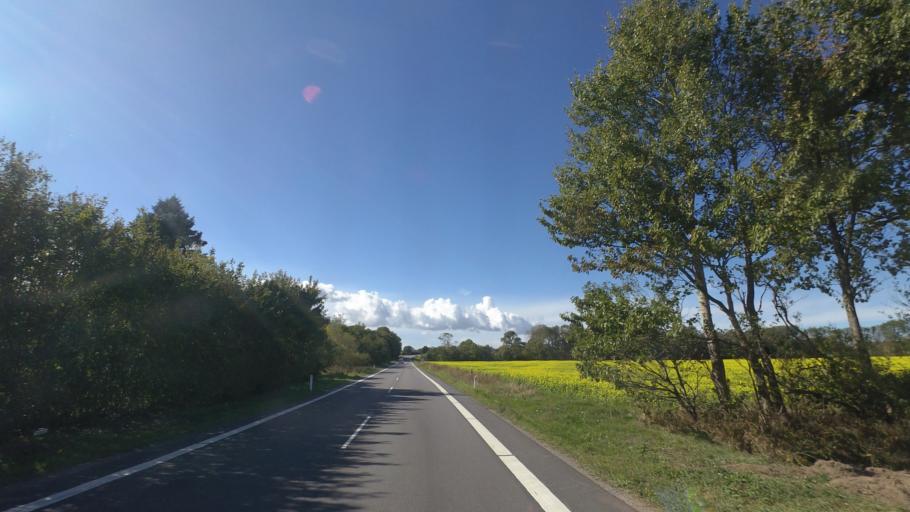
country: DK
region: Capital Region
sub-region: Bornholm Kommune
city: Akirkeby
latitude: 55.0693
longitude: 14.9813
